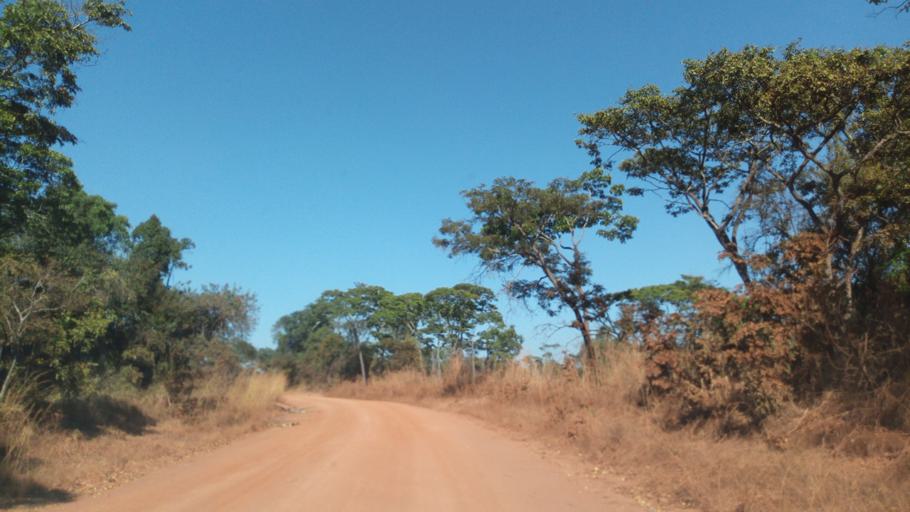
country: ZM
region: Luapula
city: Mwense
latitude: -10.6983
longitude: 28.3824
